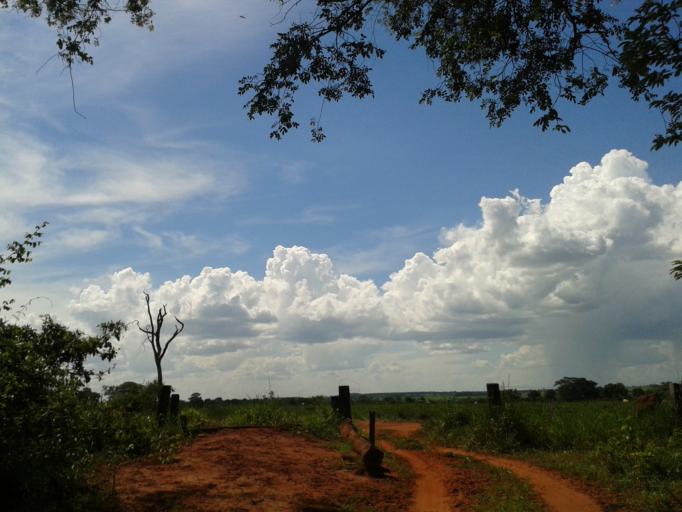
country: BR
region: Minas Gerais
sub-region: Santa Vitoria
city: Santa Vitoria
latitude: -19.1406
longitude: -50.5509
